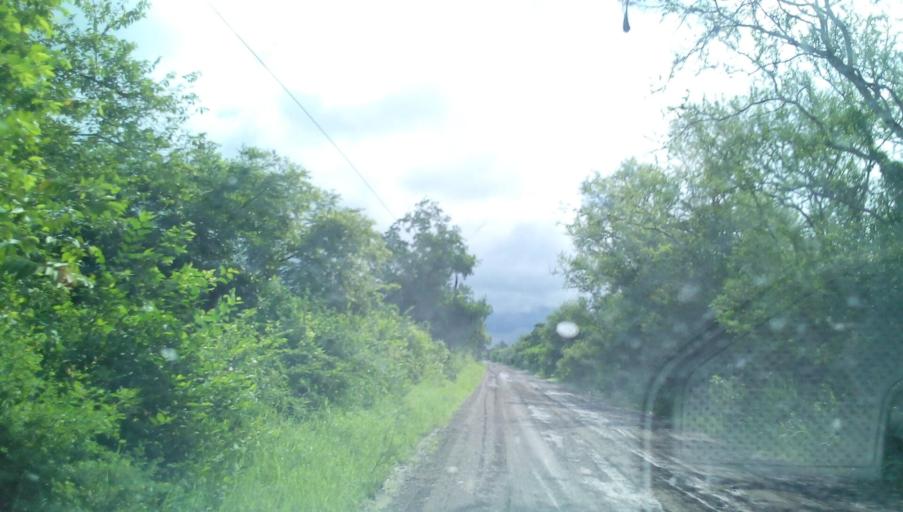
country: MX
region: Veracruz
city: Panuco
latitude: 21.8509
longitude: -98.1624
